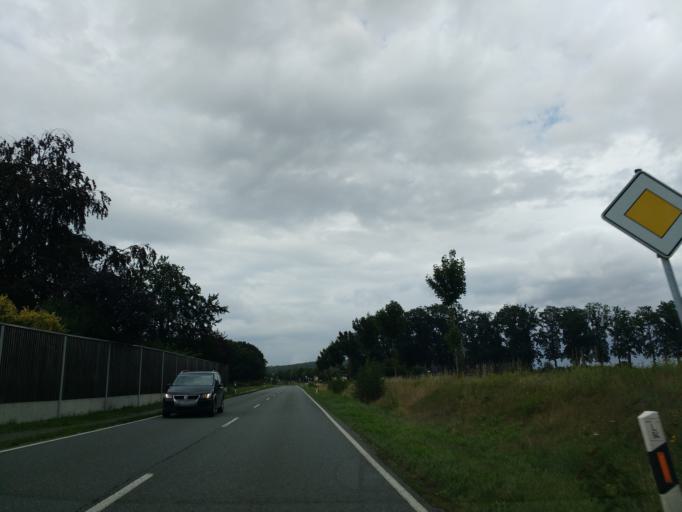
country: DE
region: Lower Saxony
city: Bad Laer
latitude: 52.0970
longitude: 8.0668
